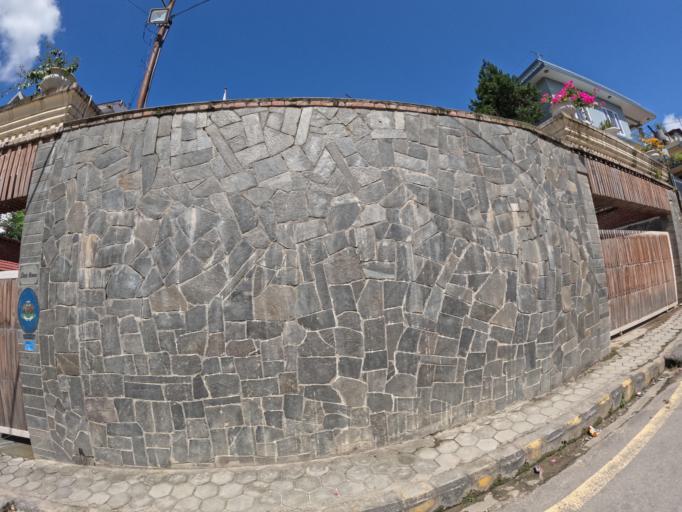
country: NP
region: Central Region
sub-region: Bagmati Zone
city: Kathmandu
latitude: 27.7505
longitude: 85.3329
